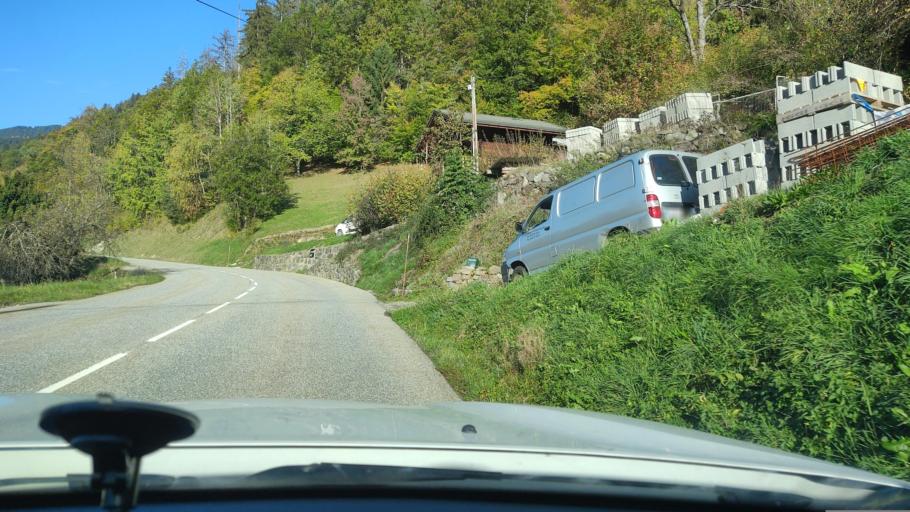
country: FR
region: Rhone-Alpes
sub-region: Departement de la Savoie
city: Beaufort
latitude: 45.7280
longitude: 6.5547
